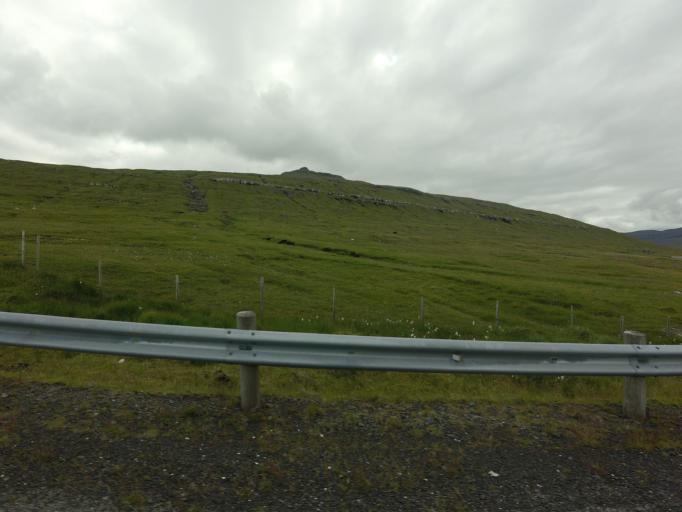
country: FO
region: Eysturoy
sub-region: Eidi
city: Eidi
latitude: 62.2104
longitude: -6.9985
